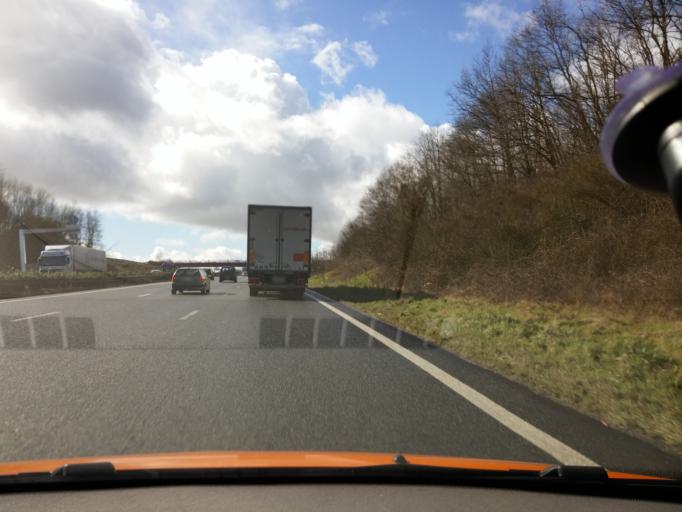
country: FR
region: Ile-de-France
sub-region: Departement de l'Essonne
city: Villejust
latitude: 48.6934
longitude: 2.2285
